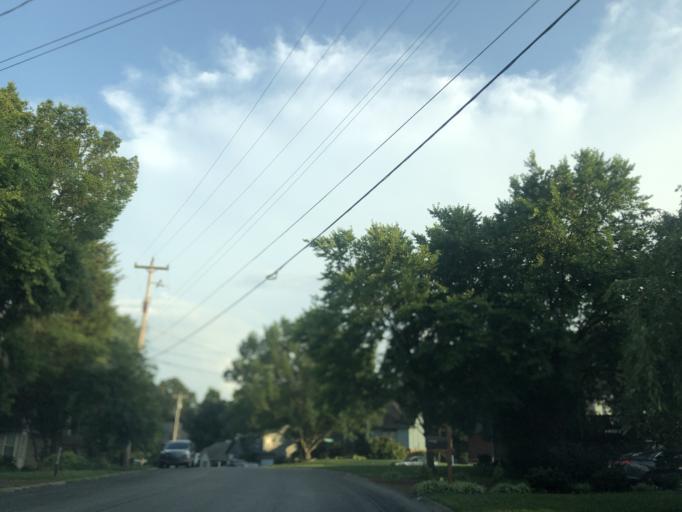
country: US
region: Tennessee
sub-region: Davidson County
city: Lakewood
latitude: 36.1363
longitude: -86.6368
